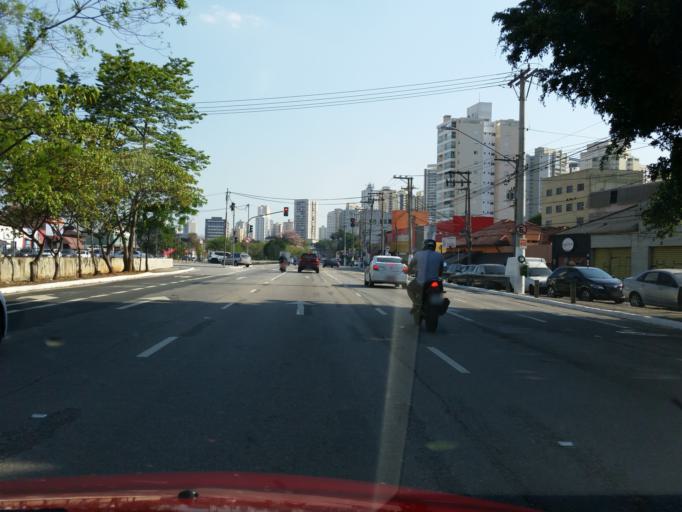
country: BR
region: Sao Paulo
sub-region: Sao Paulo
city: Sao Paulo
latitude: -23.6051
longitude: -46.6265
